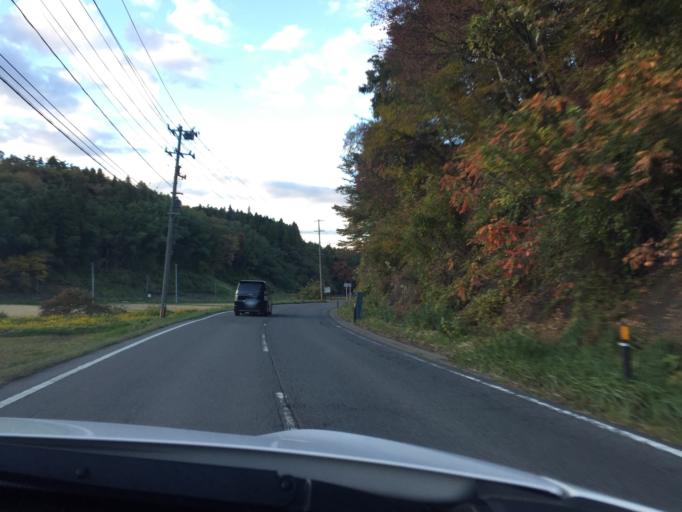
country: JP
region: Fukushima
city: Ishikawa
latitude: 37.2087
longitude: 140.6262
